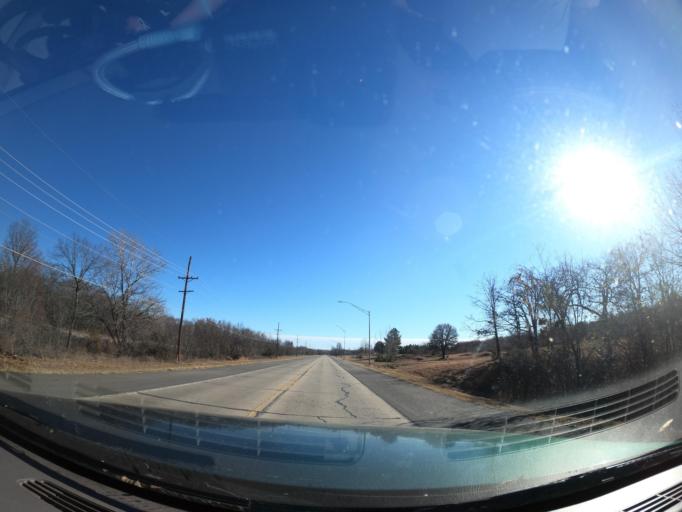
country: US
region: Oklahoma
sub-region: McIntosh County
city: Eufaula
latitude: 35.3046
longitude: -95.5869
